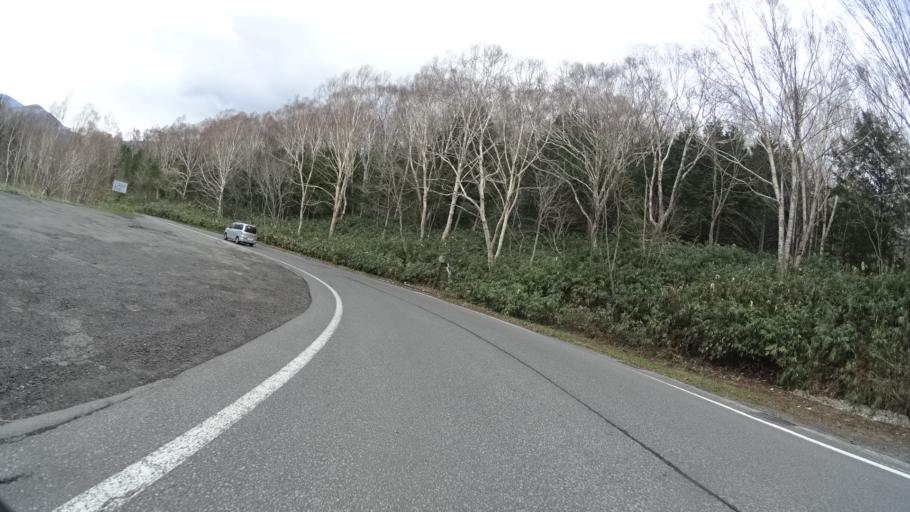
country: JP
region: Nagano
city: Nakano
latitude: 36.7118
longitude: 138.4949
